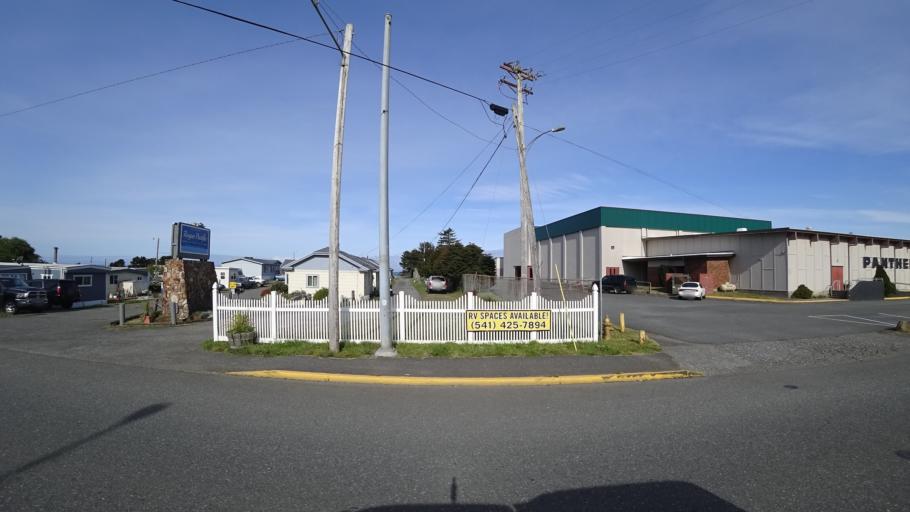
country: US
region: Oregon
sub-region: Curry County
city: Gold Beach
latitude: 42.4076
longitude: -124.4210
